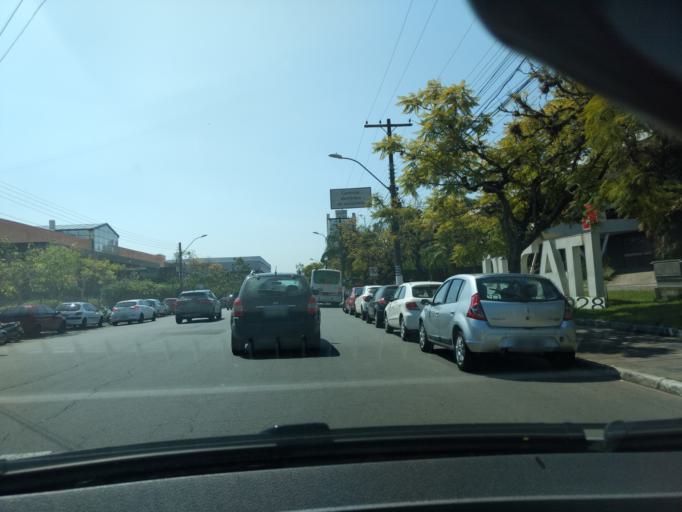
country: BR
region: Rio Grande do Sul
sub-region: Porto Alegre
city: Porto Alegre
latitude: -30.0269
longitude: -51.1612
